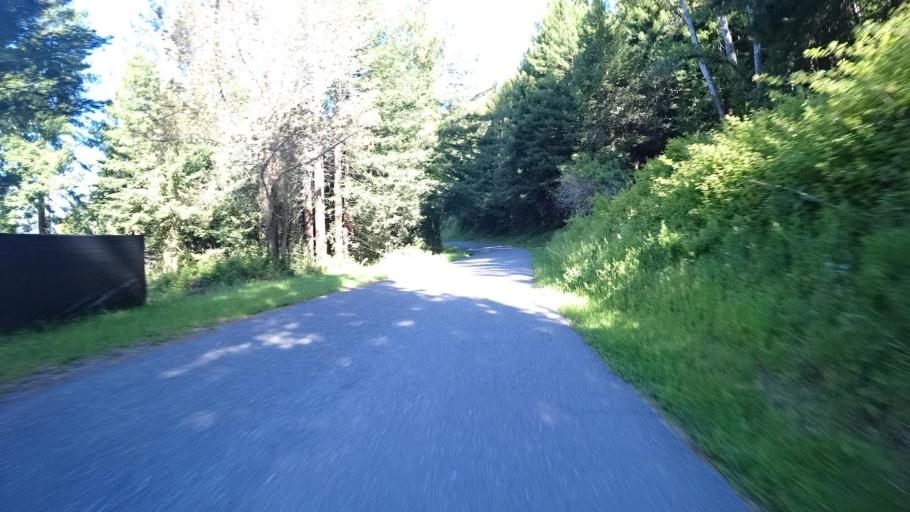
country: US
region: California
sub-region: Humboldt County
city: Rio Dell
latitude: 40.4546
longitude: -123.9901
